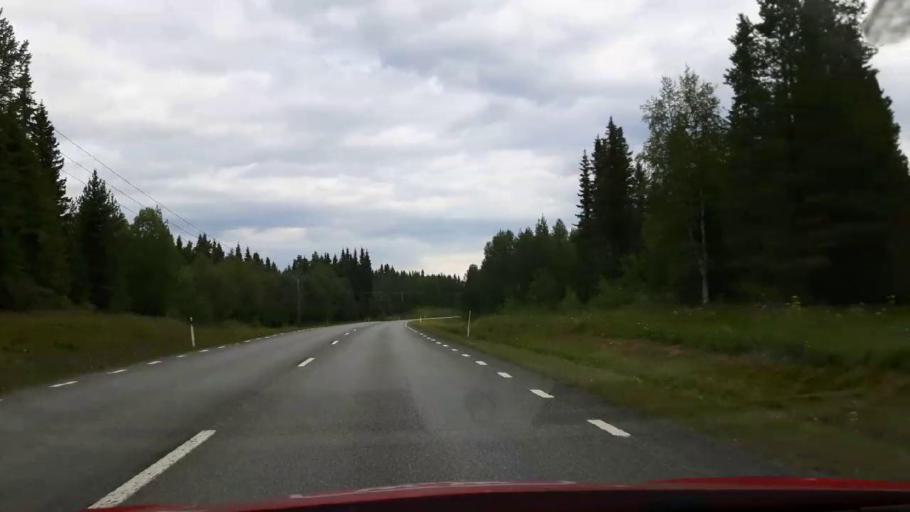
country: SE
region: Jaemtland
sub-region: Stroemsunds Kommun
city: Stroemsund
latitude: 63.6451
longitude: 15.3736
